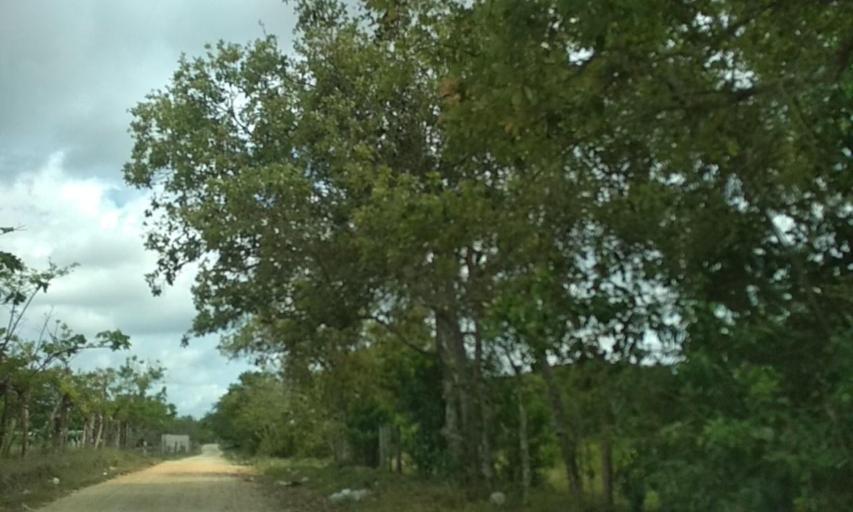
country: MX
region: Veracruz
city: Las Choapas
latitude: 17.8981
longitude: -94.1194
